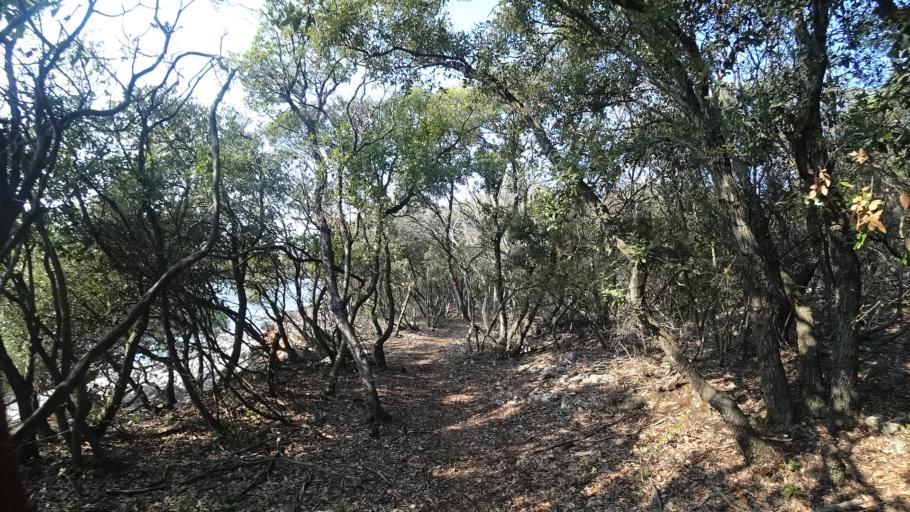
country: HR
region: Primorsko-Goranska
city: Mali Losinj
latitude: 44.4869
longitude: 14.5090
